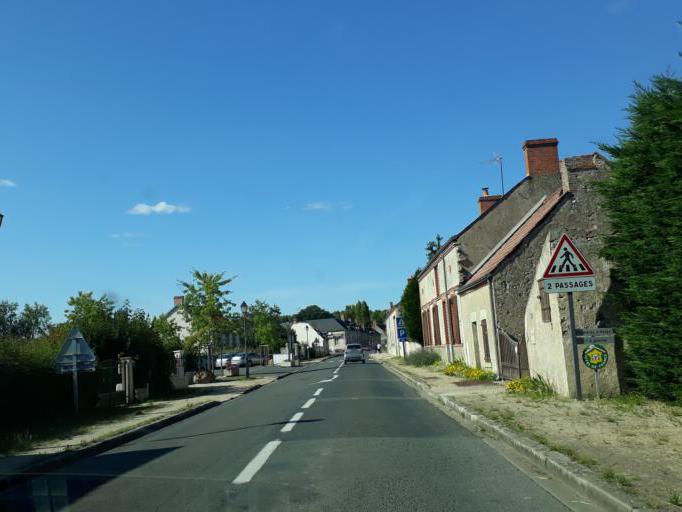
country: FR
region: Centre
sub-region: Departement du Loiret
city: Chateauneuf-sur-Loire
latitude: 47.8443
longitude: 2.2664
